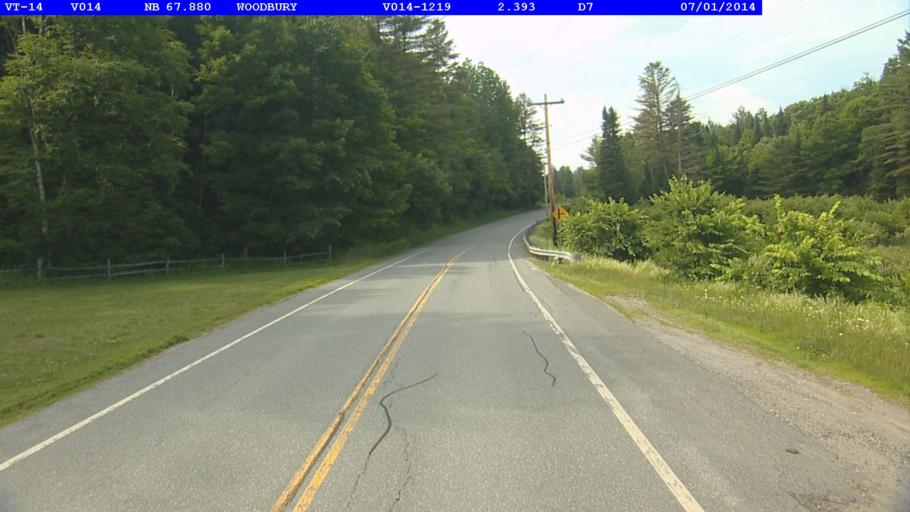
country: US
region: Vermont
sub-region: Caledonia County
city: Hardwick
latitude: 44.4229
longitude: -72.4116
